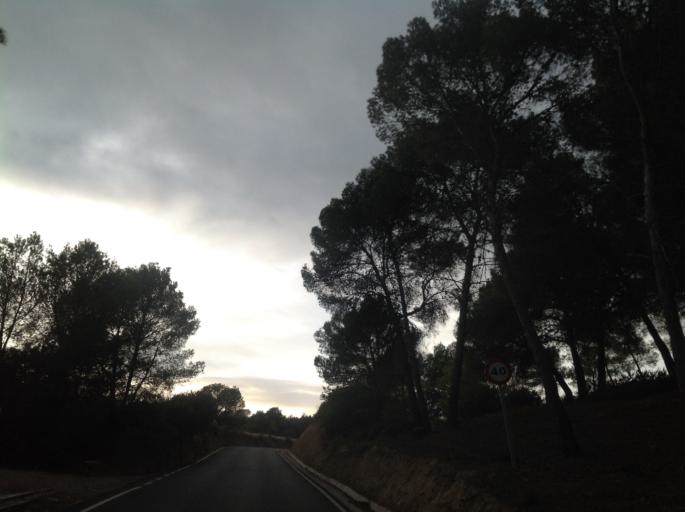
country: ES
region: Andalusia
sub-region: Provincia de Malaga
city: Ardales
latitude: 36.9102
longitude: -4.8006
